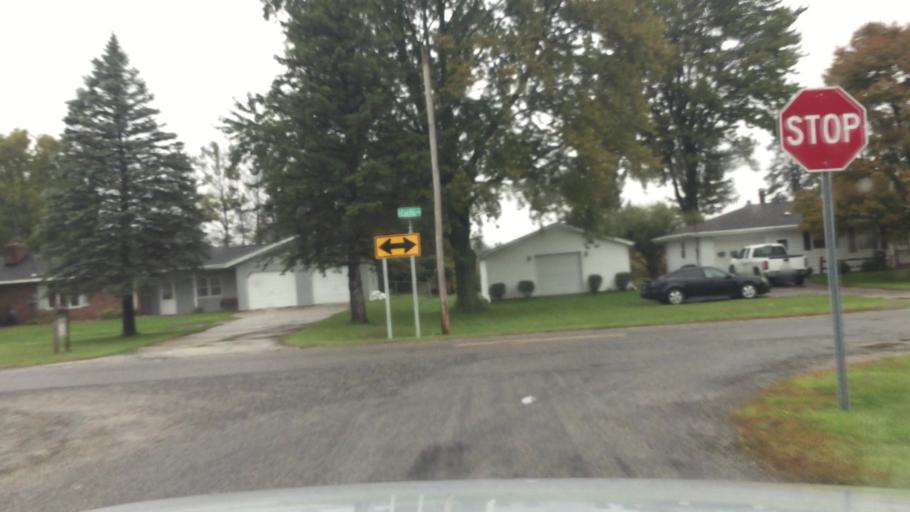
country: US
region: Michigan
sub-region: Saginaw County
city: Bridgeport
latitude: 43.3215
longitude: -83.8355
